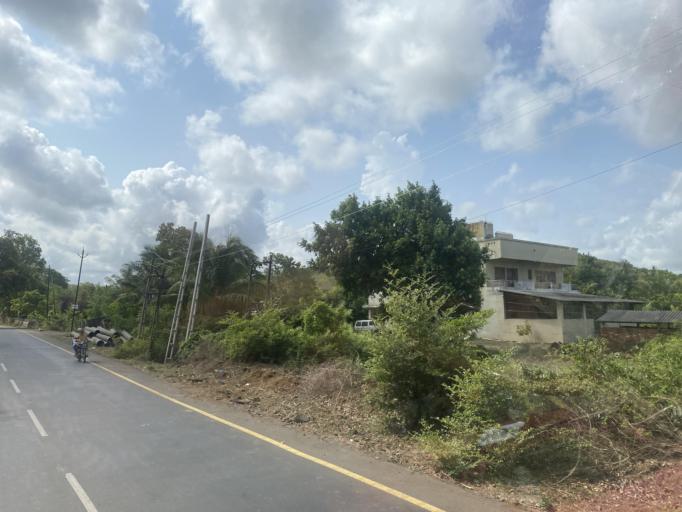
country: IN
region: Gujarat
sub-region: Valsad
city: Vapi
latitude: 20.3204
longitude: 72.8325
